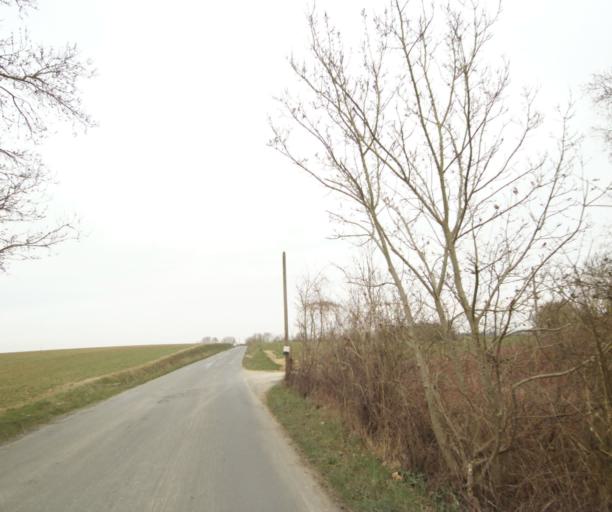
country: FR
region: Poitou-Charentes
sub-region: Departement des Deux-Sevres
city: Bessines
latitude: 46.3077
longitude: -0.5164
